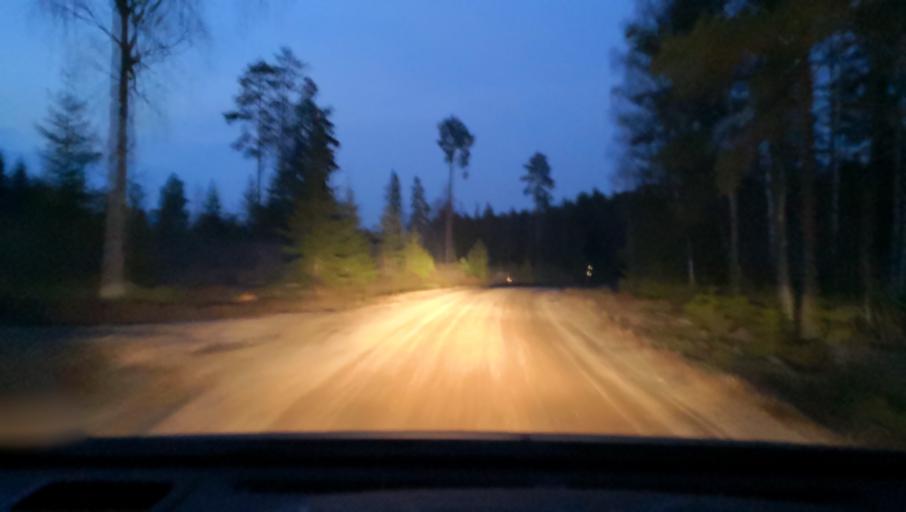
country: SE
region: OErebro
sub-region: Lindesbergs Kommun
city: Frovi
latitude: 59.5991
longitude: 15.4660
